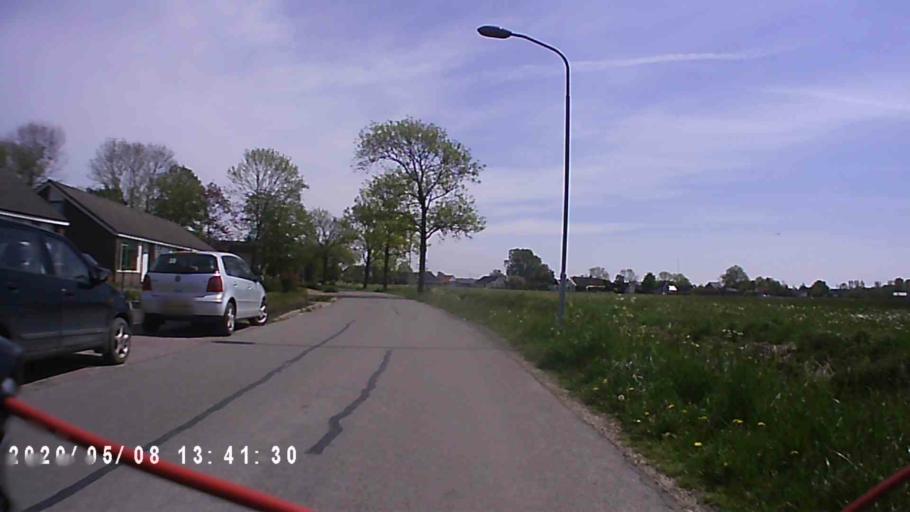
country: NL
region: Groningen
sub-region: Gemeente Appingedam
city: Appingedam
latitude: 53.3212
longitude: 6.7811
